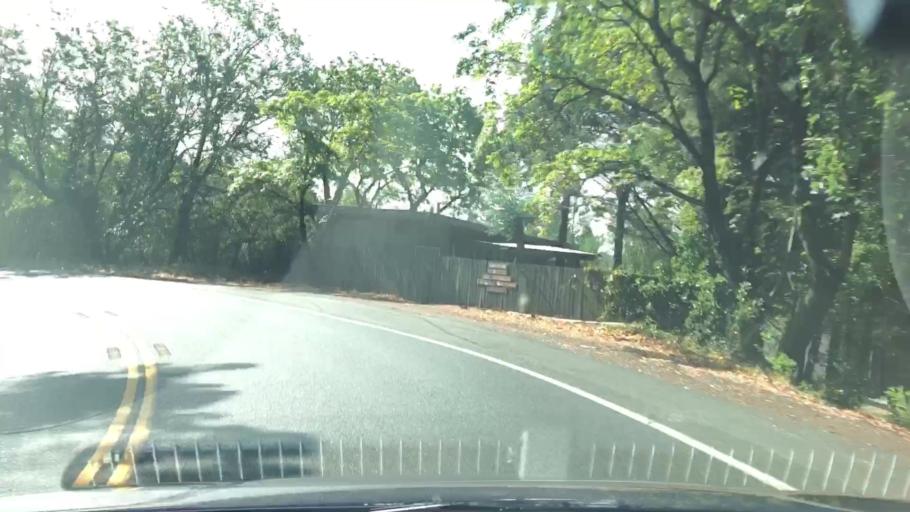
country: US
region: California
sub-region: Napa County
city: Calistoga
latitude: 38.6441
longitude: -122.5932
